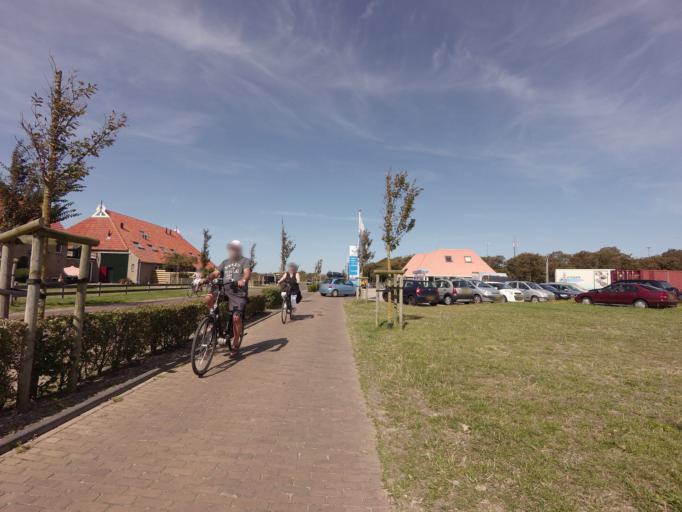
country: NL
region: Friesland
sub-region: Gemeente Ameland
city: Hollum
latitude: 53.4439
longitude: 5.6352
